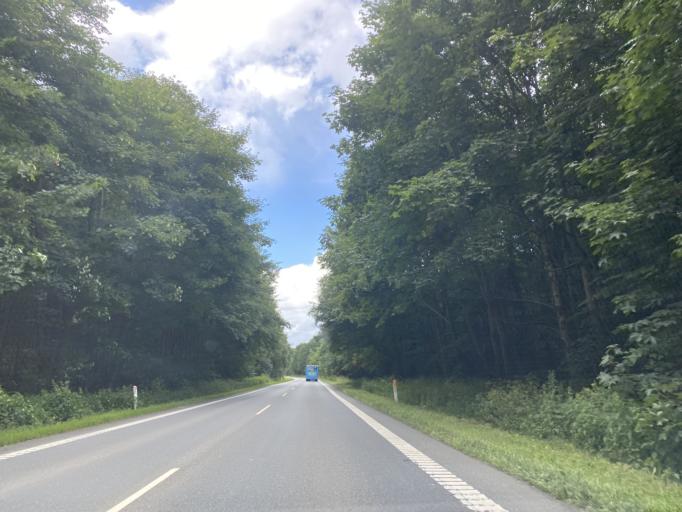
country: DK
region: Central Jutland
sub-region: Silkeborg Kommune
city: Silkeborg
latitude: 56.2601
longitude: 9.6242
